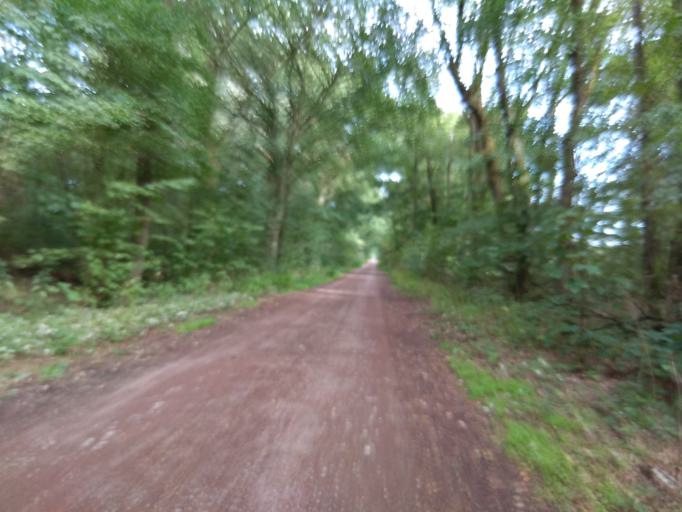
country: DE
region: North Rhine-Westphalia
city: Marl
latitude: 51.7101
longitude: 7.0548
